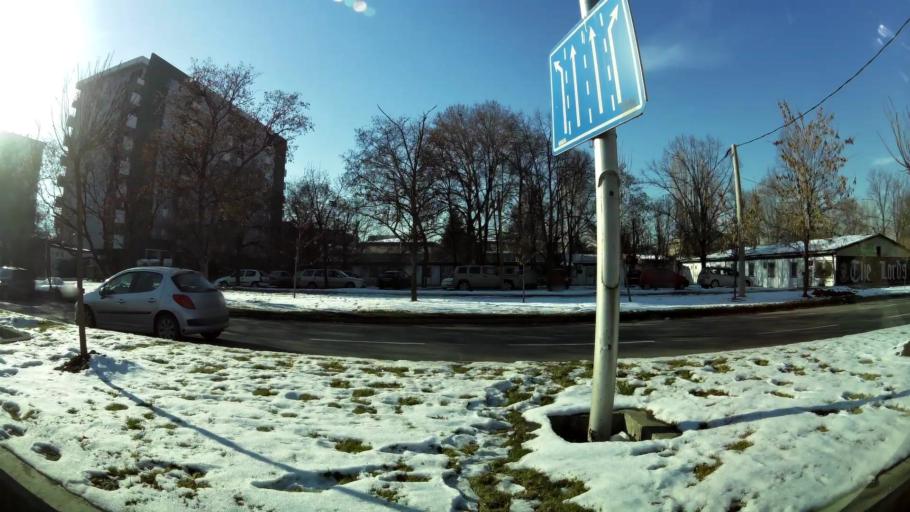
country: MK
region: Karpos
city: Skopje
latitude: 42.0010
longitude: 21.4045
